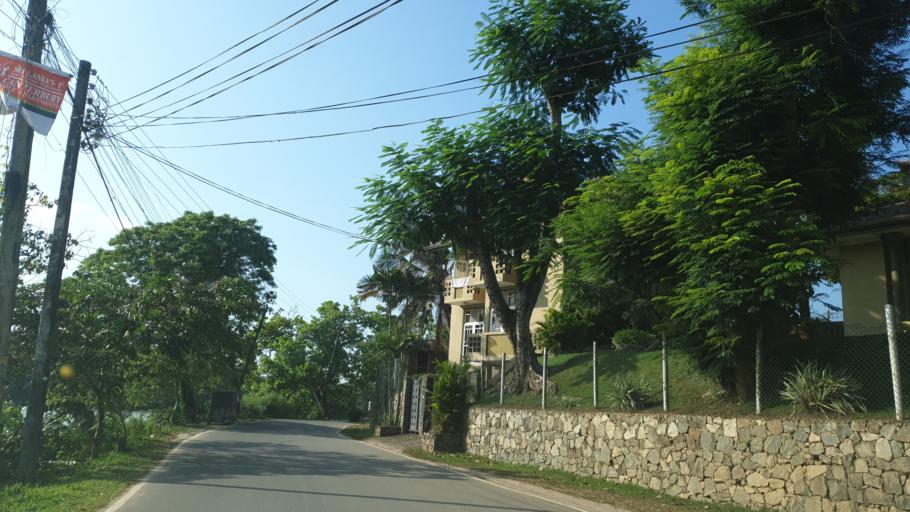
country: LK
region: Western
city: Battaramulla South
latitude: 6.8872
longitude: 79.9482
